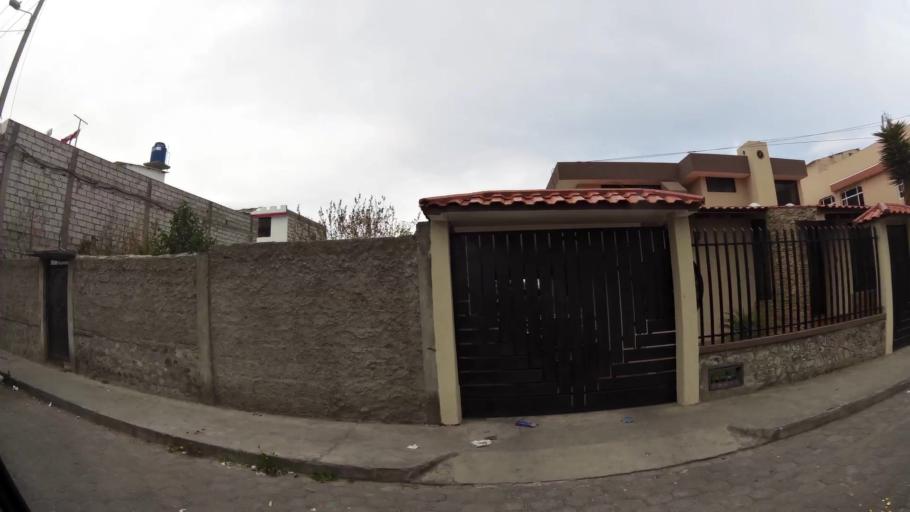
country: EC
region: Cotopaxi
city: Latacunga
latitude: -0.9306
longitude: -78.6089
